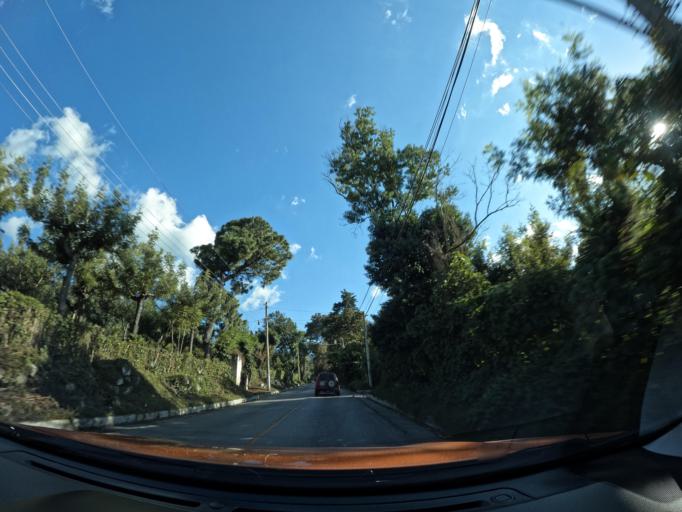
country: GT
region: Sacatepequez
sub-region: Municipio de Santa Maria de Jesus
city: Santa Maria de Jesus
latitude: 14.5290
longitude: -90.7270
